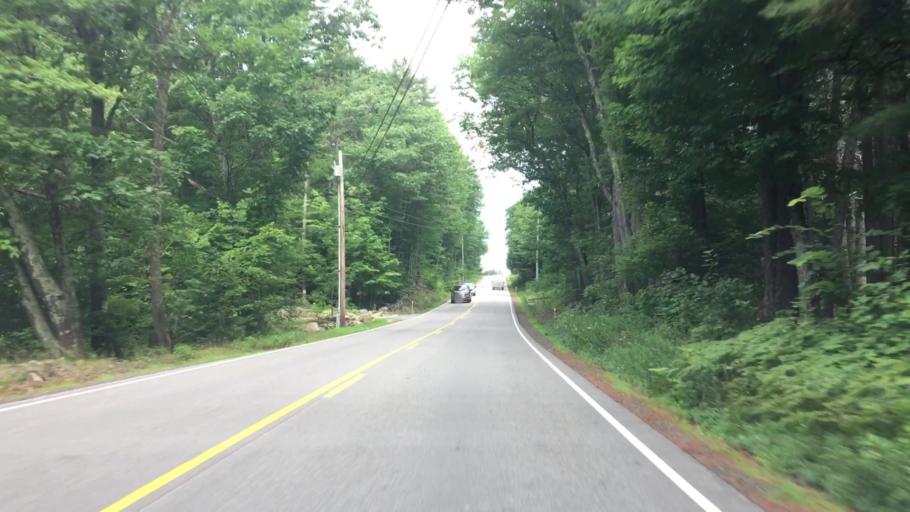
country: US
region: New Hampshire
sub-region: Belknap County
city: Laconia
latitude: 43.5821
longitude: -71.5142
